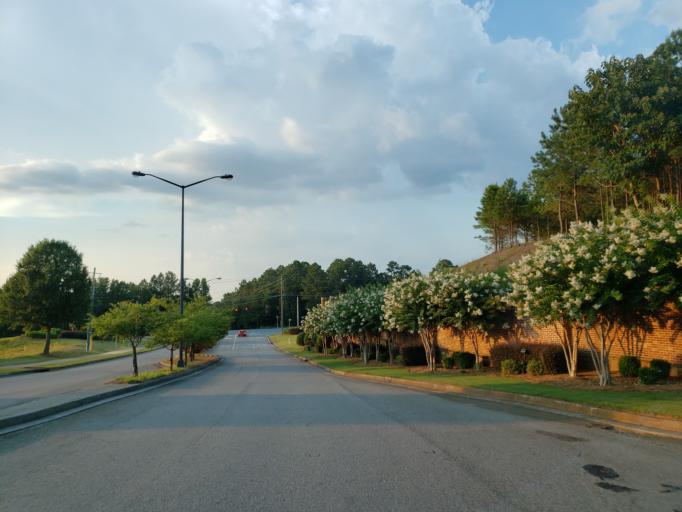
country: US
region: Georgia
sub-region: Bartow County
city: Cartersville
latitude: 34.1159
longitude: -84.8209
